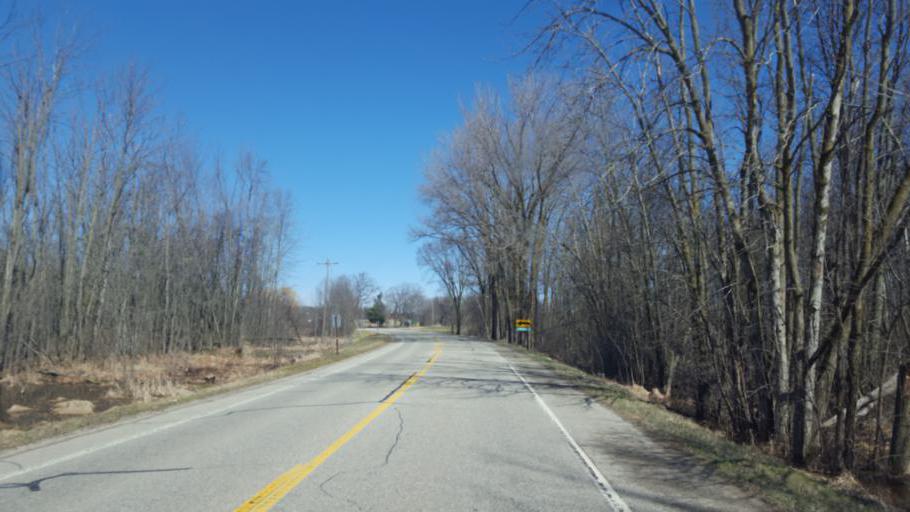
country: US
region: Michigan
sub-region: Montcalm County
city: Edmore
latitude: 43.4643
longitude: -85.0442
